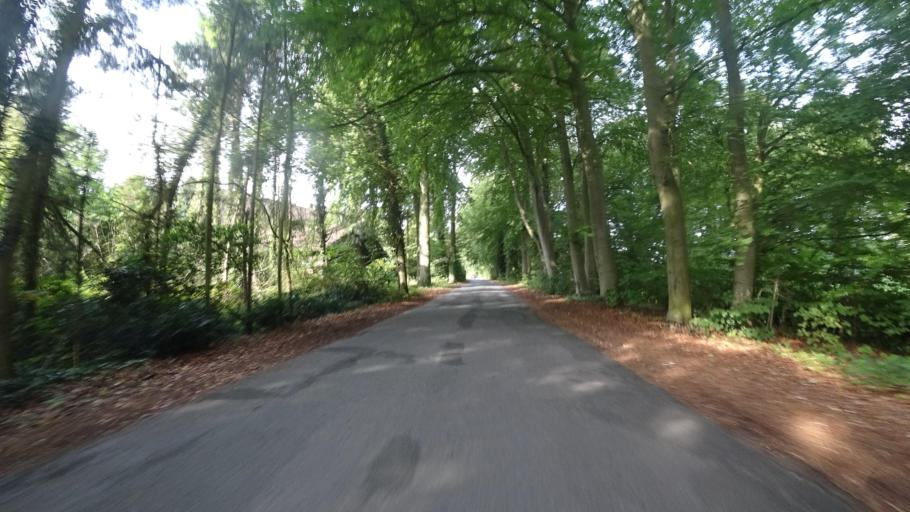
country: DE
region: North Rhine-Westphalia
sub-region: Regierungsbezirk Detmold
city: Steinhagen
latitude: 51.9499
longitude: 8.4198
